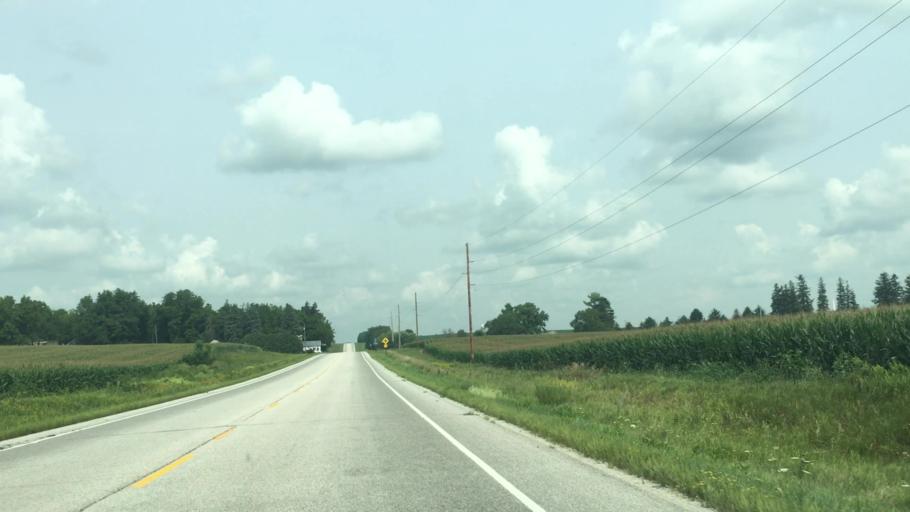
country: US
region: Minnesota
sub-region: Fillmore County
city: Harmony
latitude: 43.5911
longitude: -91.9298
